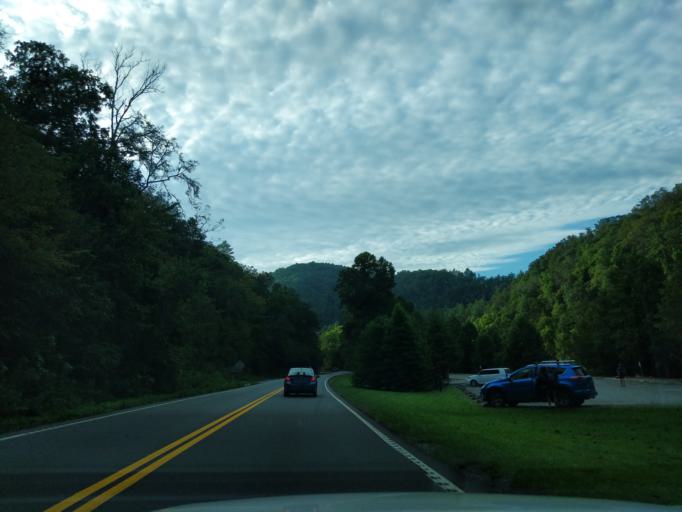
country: US
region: Tennessee
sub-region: Polk County
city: Benton
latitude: 35.0976
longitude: -84.5490
